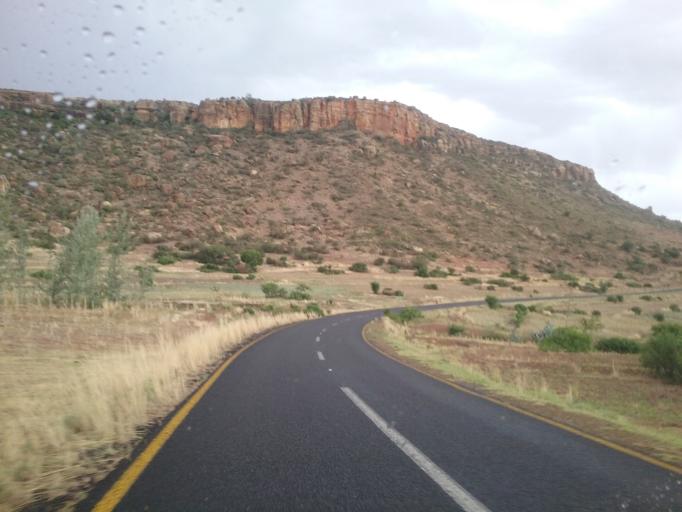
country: LS
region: Quthing
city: Quthing
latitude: -30.3076
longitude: 27.7410
